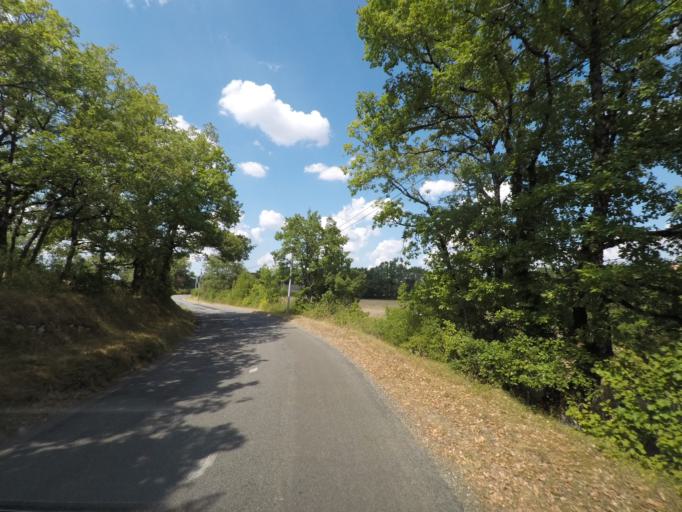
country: FR
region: Midi-Pyrenees
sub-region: Departement du Lot
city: Le Vigan
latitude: 44.6070
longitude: 1.5890
